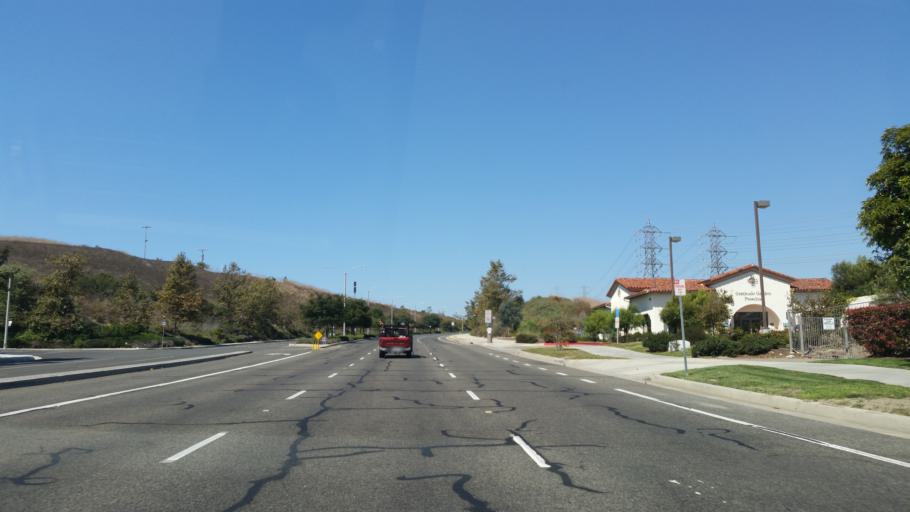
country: US
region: California
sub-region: Orange County
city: San Clemente
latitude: 33.4574
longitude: -117.6015
